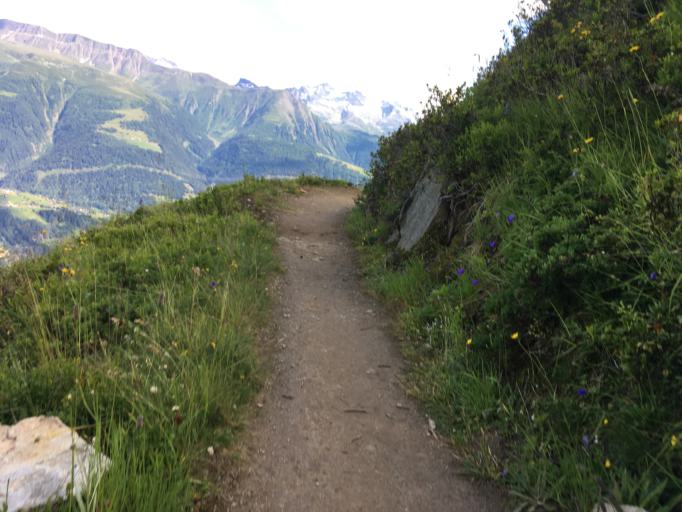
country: CH
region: Valais
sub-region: Goms District
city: Fiesch
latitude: 46.4375
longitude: 8.1196
